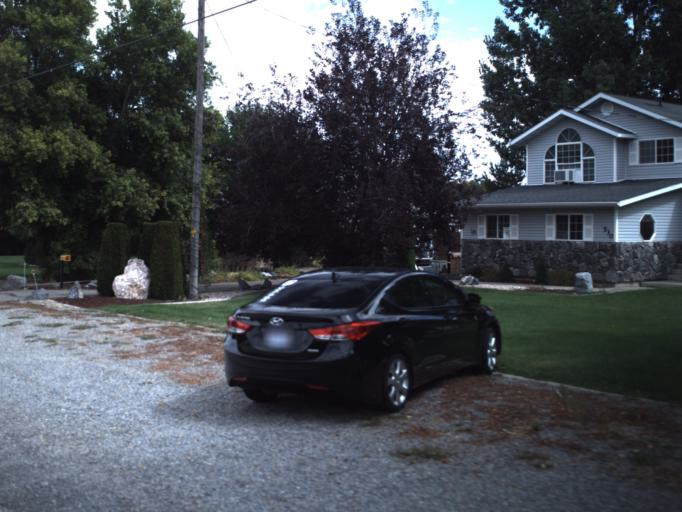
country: US
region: Utah
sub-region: Cache County
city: Wellsville
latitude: 41.6275
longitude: -111.9347
